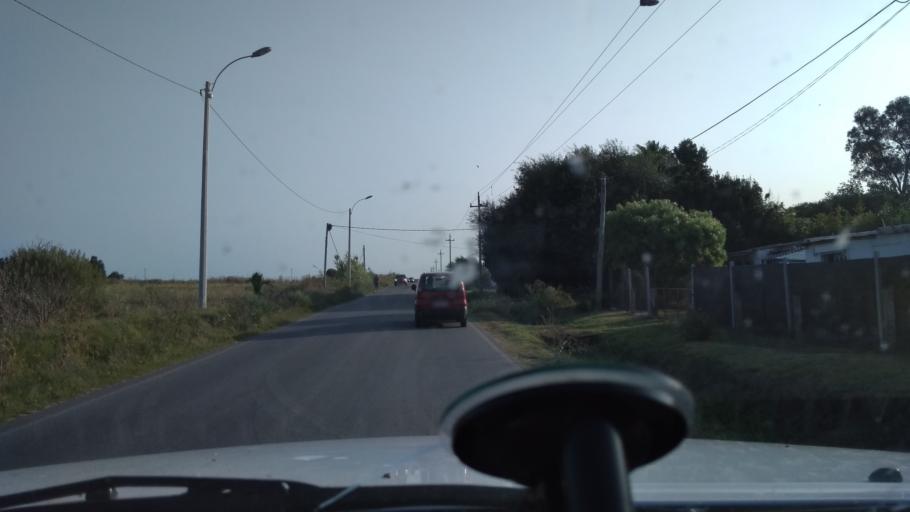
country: UY
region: Canelones
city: Colonia Nicolich
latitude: -34.7794
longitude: -56.0186
